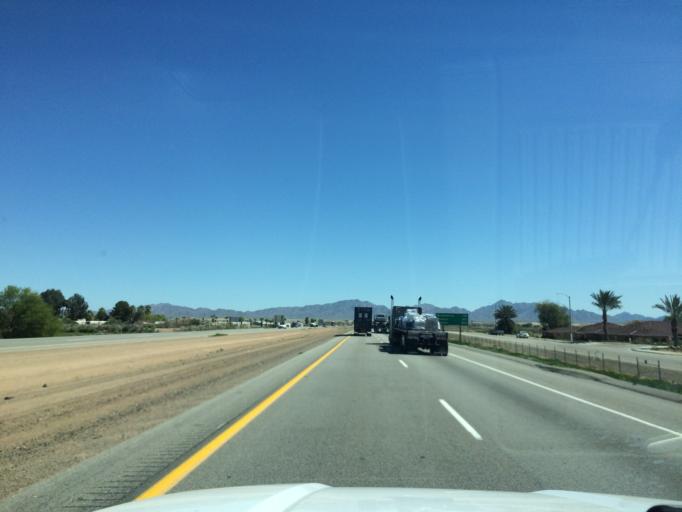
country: US
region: California
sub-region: Riverside County
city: Blythe
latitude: 33.6075
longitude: -114.5644
